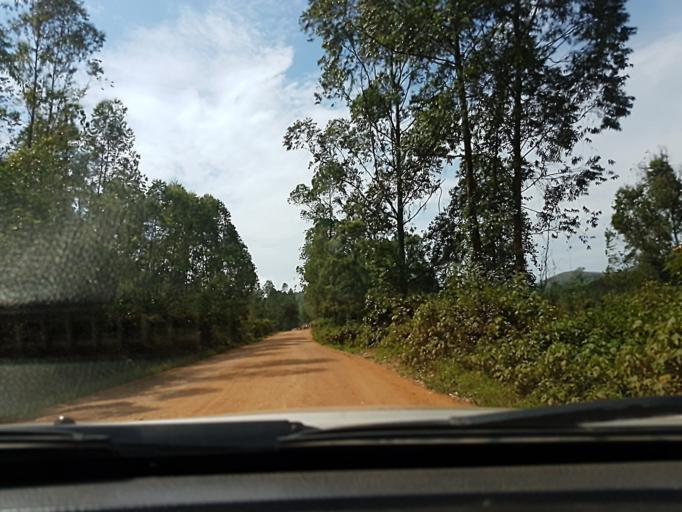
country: CD
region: South Kivu
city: Bukavu
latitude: -2.6385
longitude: 28.8754
